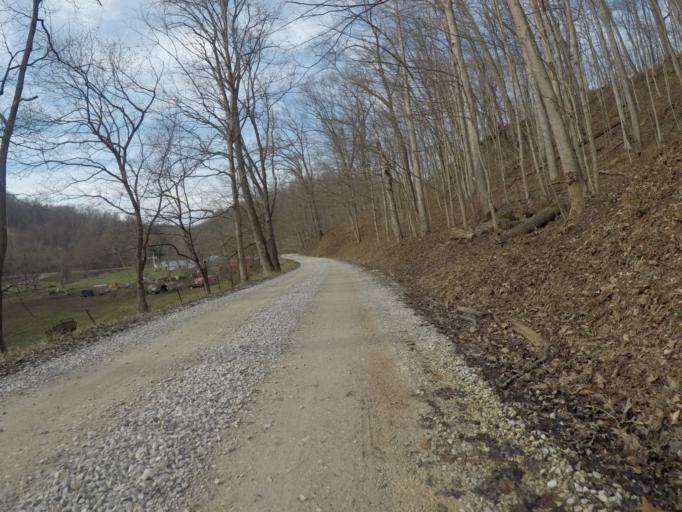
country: US
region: Ohio
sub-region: Lawrence County
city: Burlington
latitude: 38.4657
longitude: -82.5373
